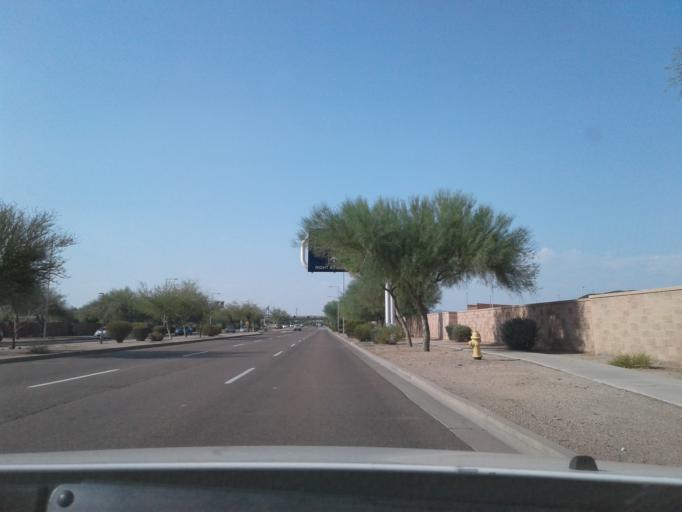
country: US
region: Arizona
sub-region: Maricopa County
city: Phoenix
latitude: 33.4331
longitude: -112.0346
